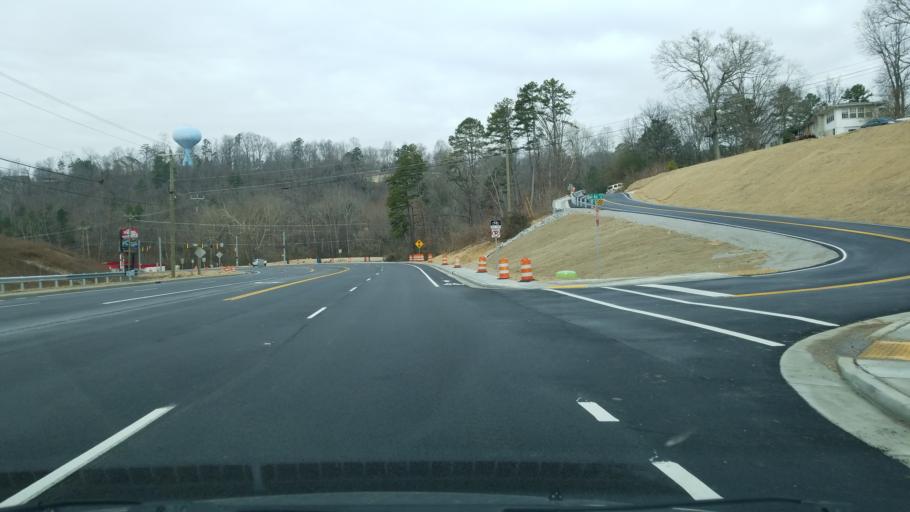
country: US
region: Tennessee
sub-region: Hamilton County
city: East Brainerd
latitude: 35.0049
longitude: -85.1185
